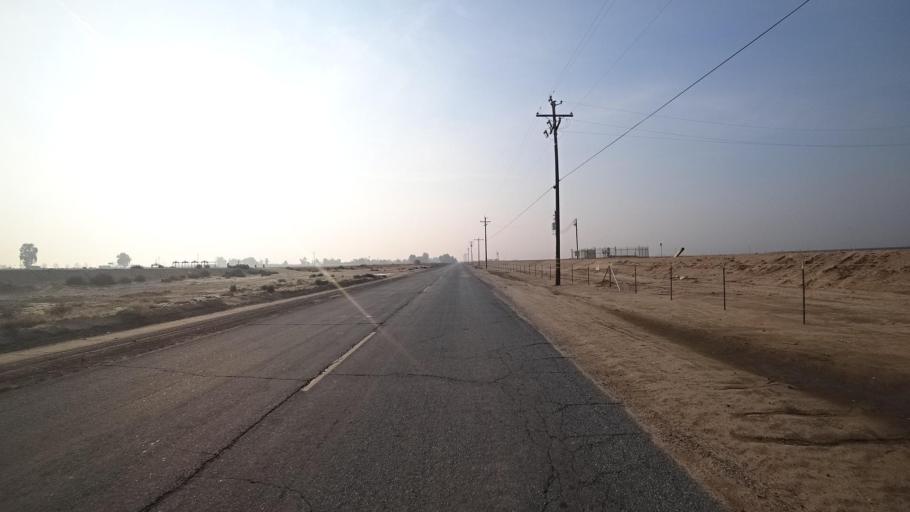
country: US
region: California
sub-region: Kern County
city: Greenfield
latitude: 35.2451
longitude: -119.0214
